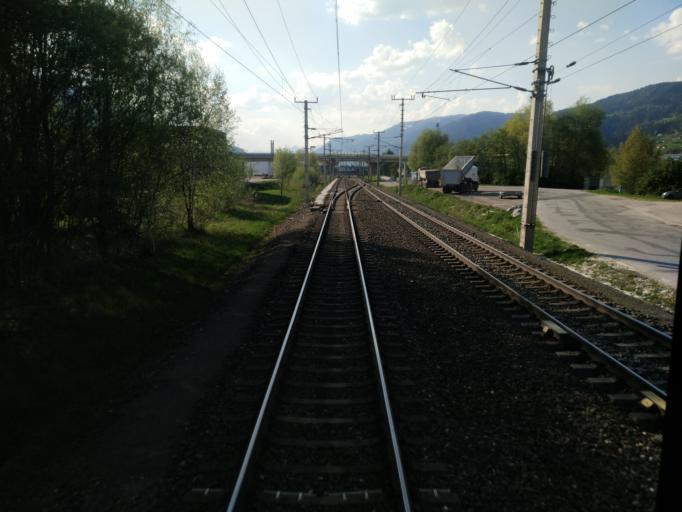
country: AT
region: Styria
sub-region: Politischer Bezirk Liezen
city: Trieben
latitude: 47.4902
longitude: 14.4862
